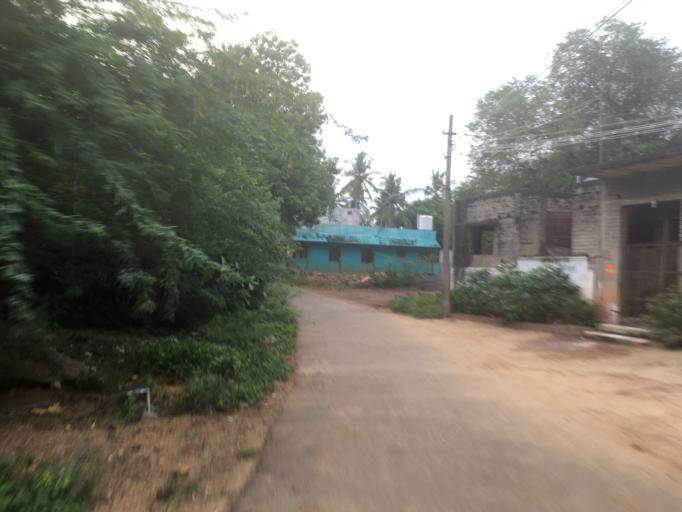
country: IN
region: Tamil Nadu
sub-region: Villupuram
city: Auroville
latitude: 12.0113
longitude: 79.8011
